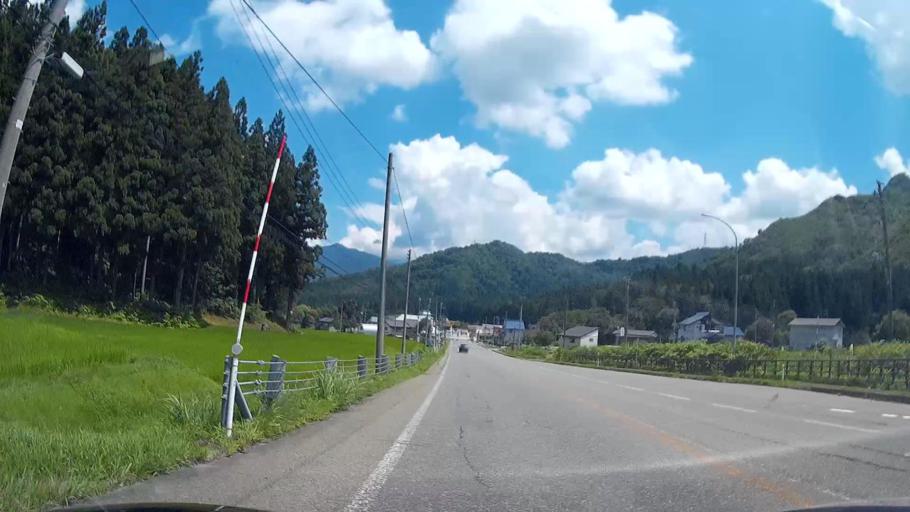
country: JP
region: Niigata
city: Shiozawa
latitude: 36.9211
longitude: 138.8176
